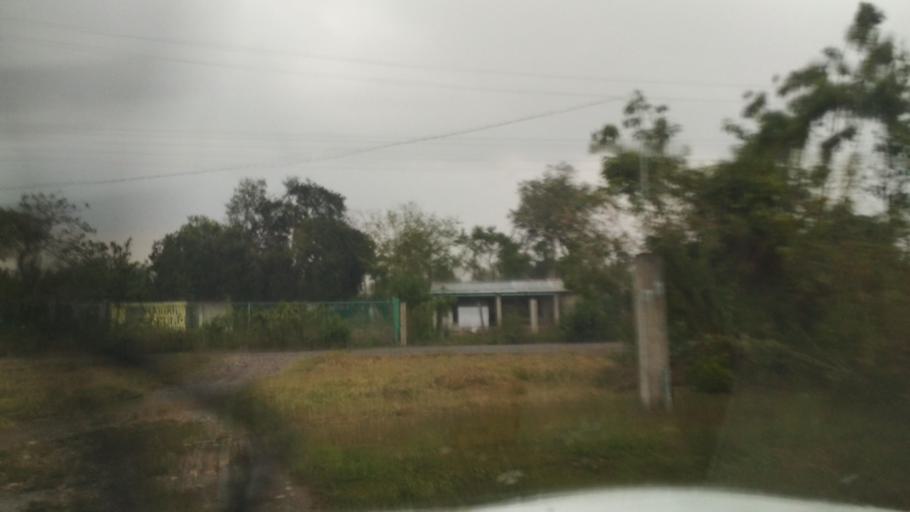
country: MM
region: Shan
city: Taunggyi
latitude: 20.3016
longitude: 97.3052
